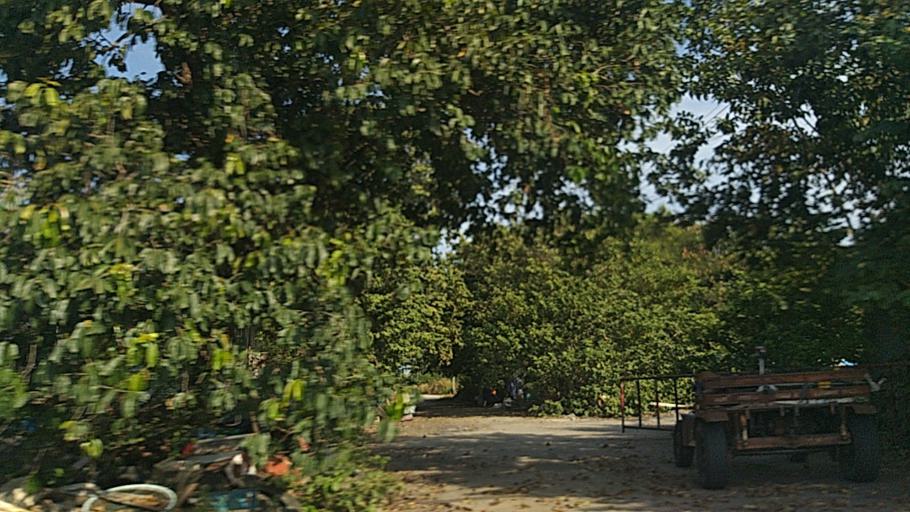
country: TH
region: Pathum Thani
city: Thanyaburi
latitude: 13.9772
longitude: 100.7289
